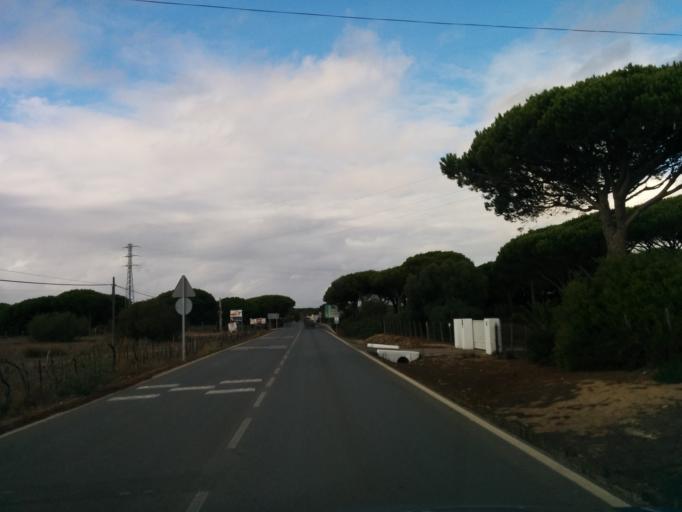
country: ES
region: Andalusia
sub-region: Provincia de Cadiz
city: Vejer de la Frontera
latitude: 36.1939
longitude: -6.0312
